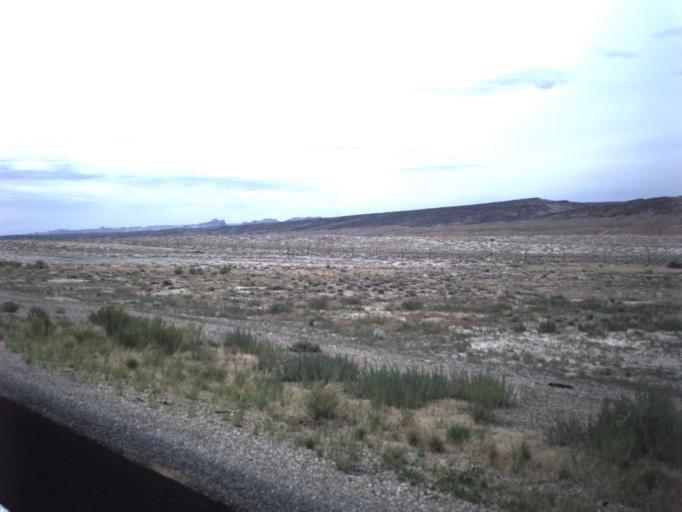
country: US
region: Utah
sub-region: Carbon County
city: East Carbon City
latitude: 39.1911
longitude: -110.3385
